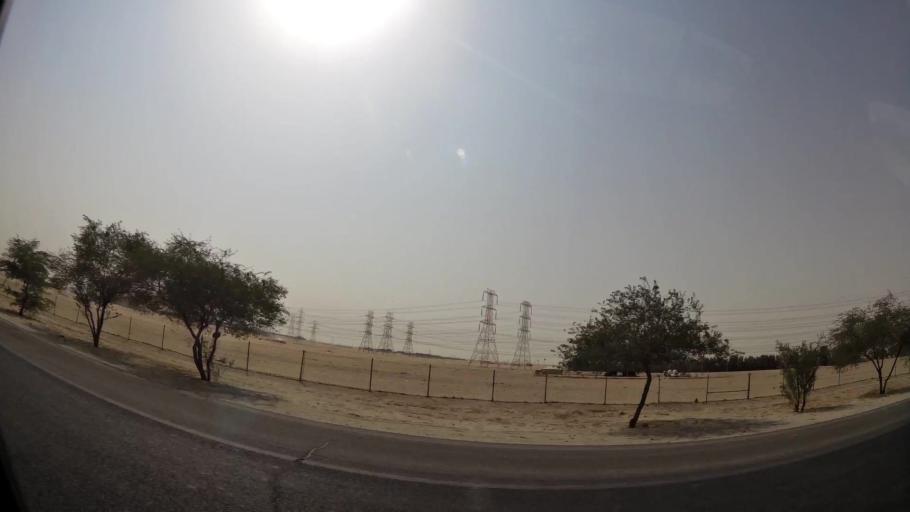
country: KW
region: Muhafazat al Jahra'
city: Al Jahra'
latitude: 29.3008
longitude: 47.6920
